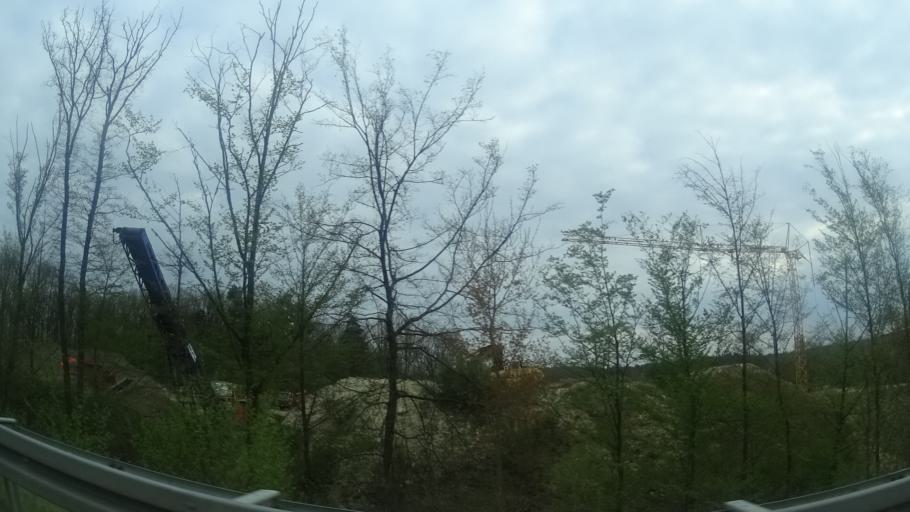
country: DE
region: Bavaria
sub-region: Upper Franconia
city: Weissenohe
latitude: 49.5767
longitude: 11.2788
